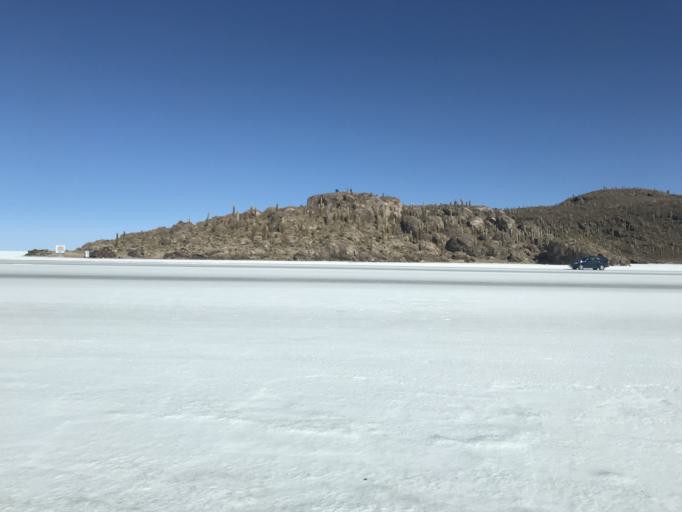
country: BO
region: Potosi
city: Colchani
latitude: -20.2381
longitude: -67.6230
